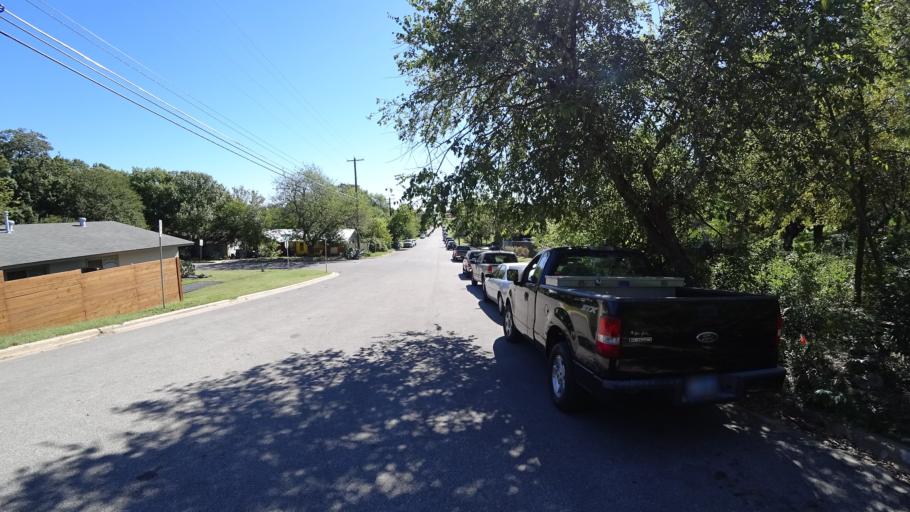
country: US
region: Texas
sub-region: Travis County
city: Austin
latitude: 30.2333
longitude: -97.7549
